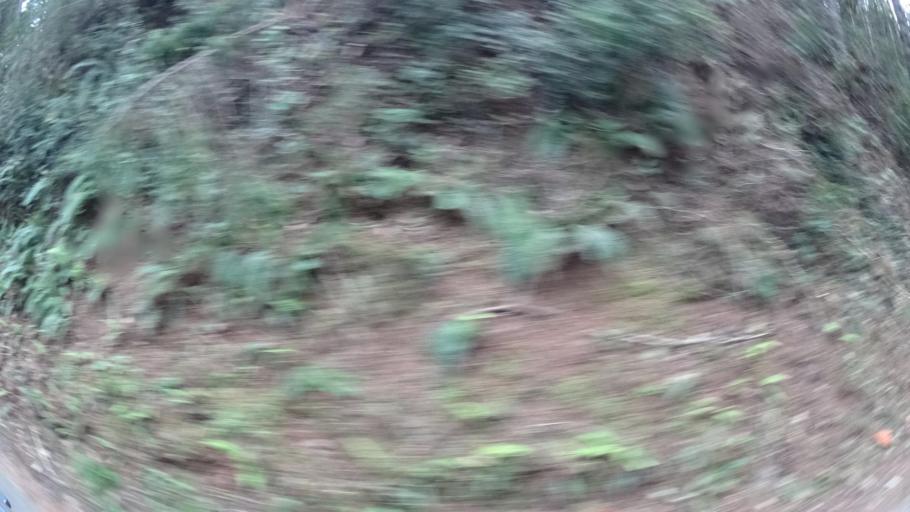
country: US
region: California
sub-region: Humboldt County
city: Redway
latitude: 40.2777
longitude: -123.7884
